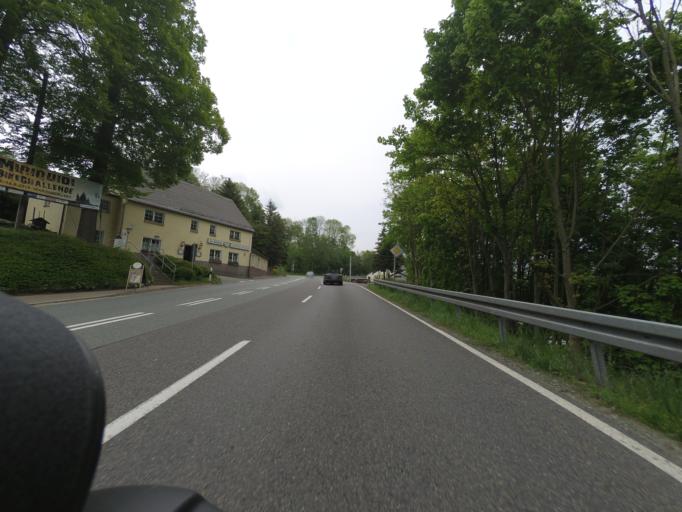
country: DE
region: Saxony
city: Grossolbersdorf
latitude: 50.7240
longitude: 13.0821
